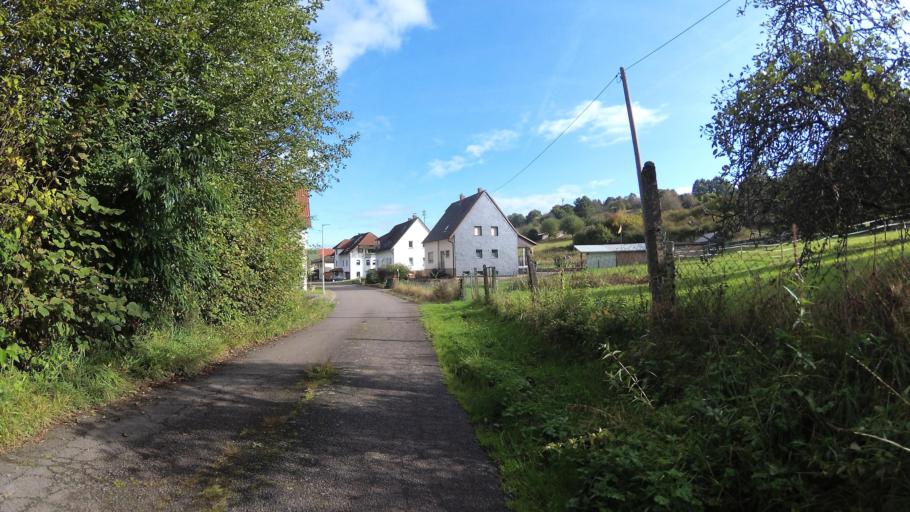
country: DE
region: Rheinland-Pfalz
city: Ohmbach
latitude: 49.4500
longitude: 7.3422
